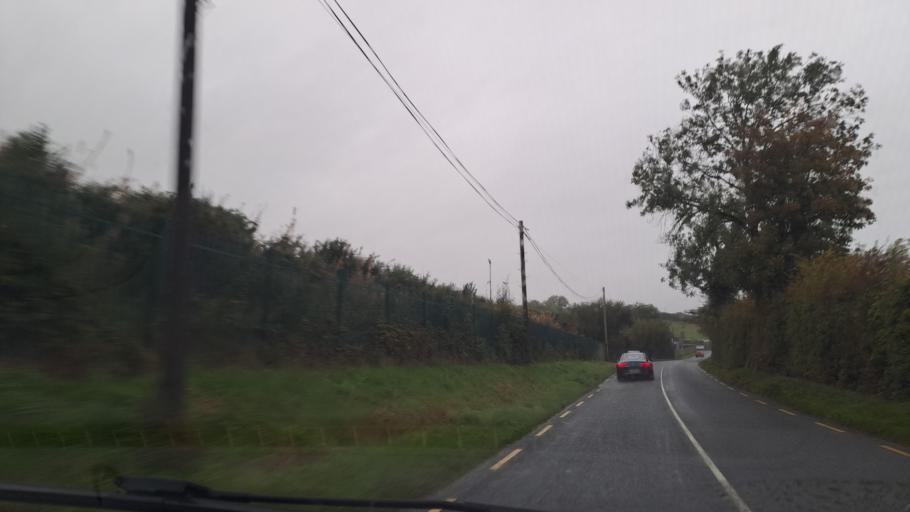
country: IE
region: Ulster
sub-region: County Monaghan
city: Monaghan
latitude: 54.2238
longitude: -6.9360
